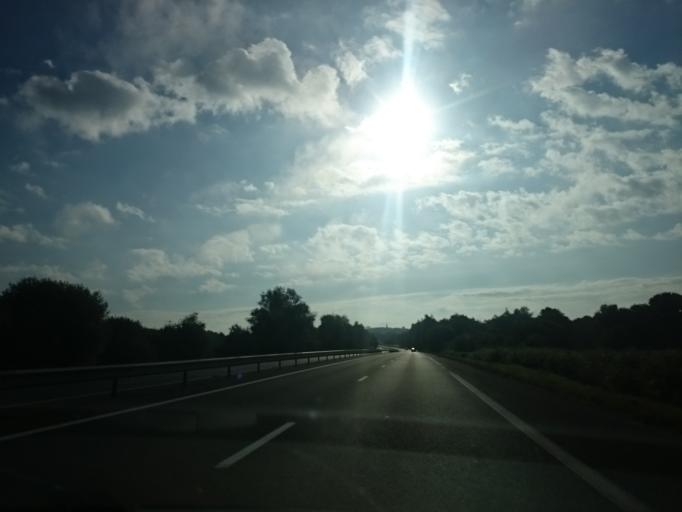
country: FR
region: Brittany
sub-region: Departement du Finistere
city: Guerlesquin
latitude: 48.5669
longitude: -3.5706
